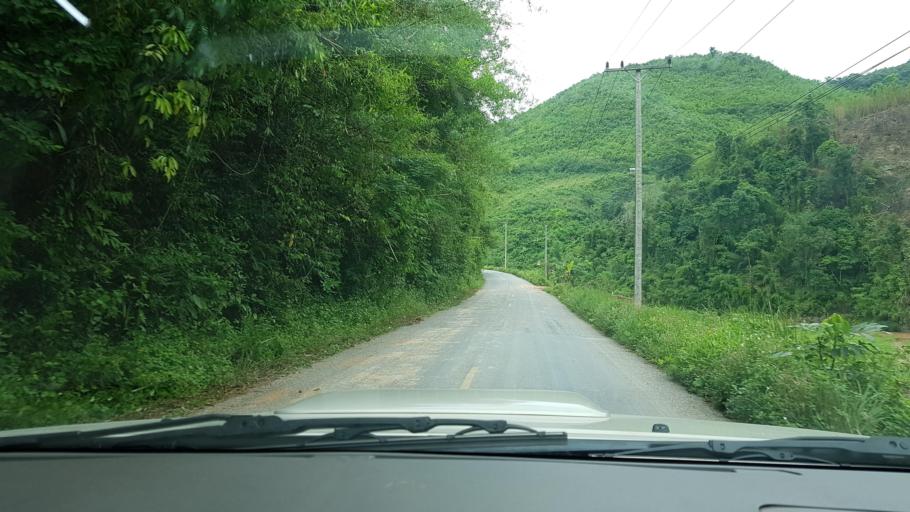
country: LA
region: Oudomxai
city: Muang La
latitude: 20.8756
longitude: 102.1494
